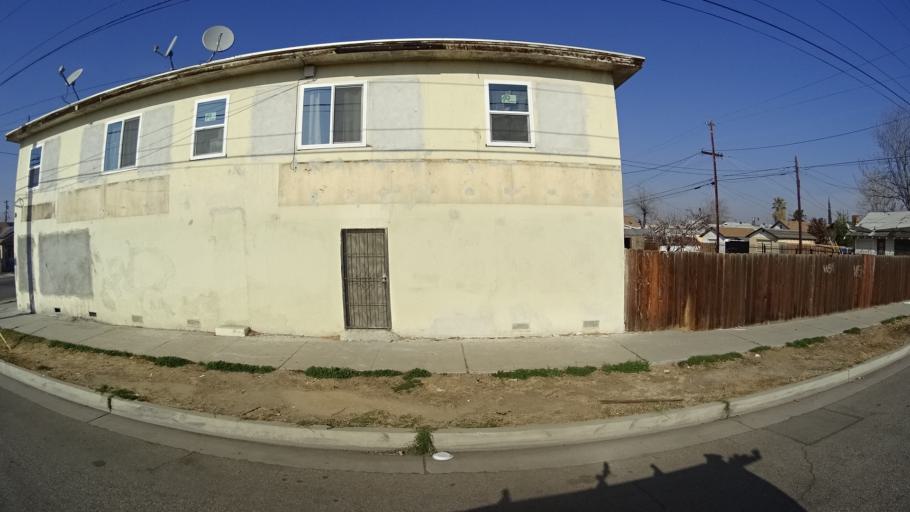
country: US
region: California
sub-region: Kern County
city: Bakersfield
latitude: 35.3646
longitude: -119.0162
